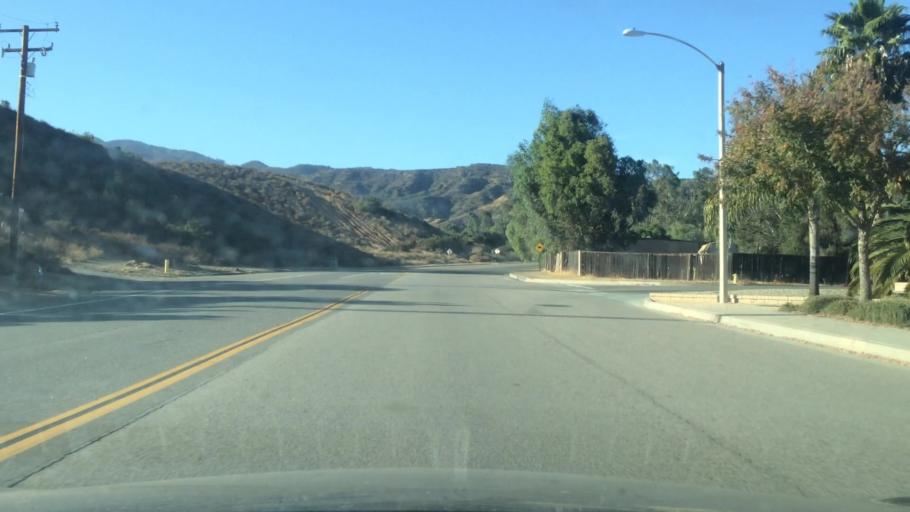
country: US
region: California
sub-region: Riverside County
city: Lakeland Village
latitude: 33.6708
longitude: -117.3960
